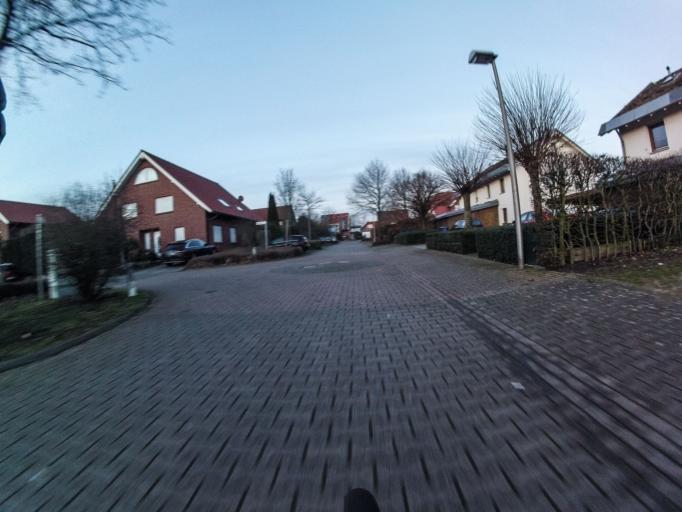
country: DE
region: North Rhine-Westphalia
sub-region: Regierungsbezirk Munster
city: Mettingen
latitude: 52.2672
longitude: 7.7934
